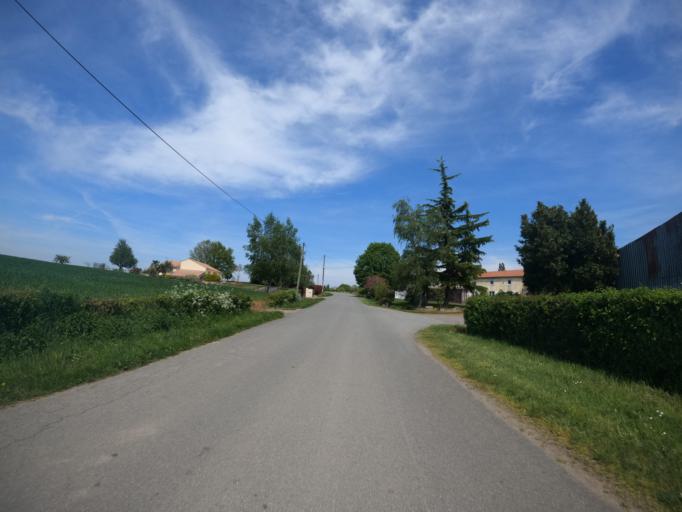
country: FR
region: Poitou-Charentes
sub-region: Departement des Deux-Sevres
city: La Chapelle-Saint-Laurent
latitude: 46.6626
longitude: -0.5072
